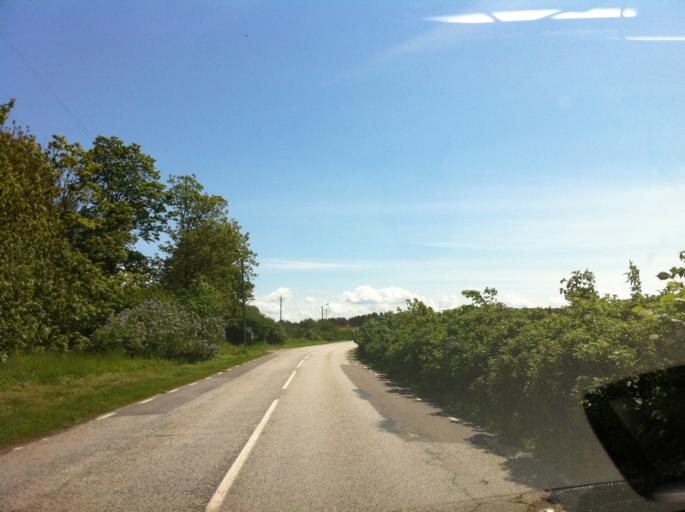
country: SE
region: Skane
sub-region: Kavlinge Kommun
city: Hofterup
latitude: 55.8290
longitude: 12.9651
